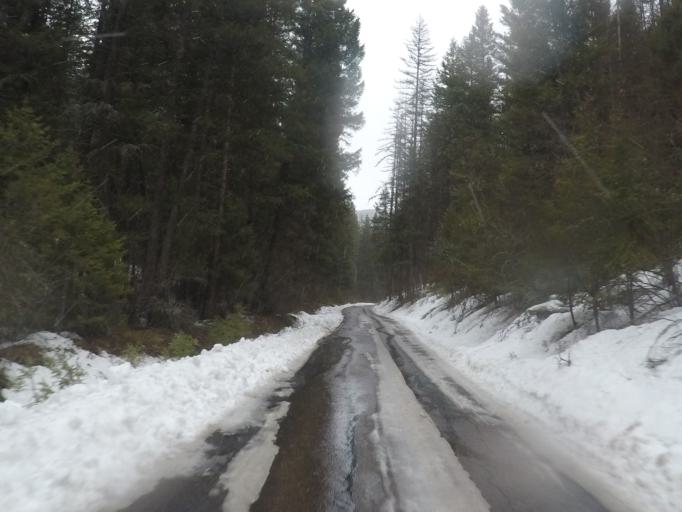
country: US
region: Montana
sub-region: Missoula County
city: Missoula
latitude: 46.9305
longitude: -113.9706
